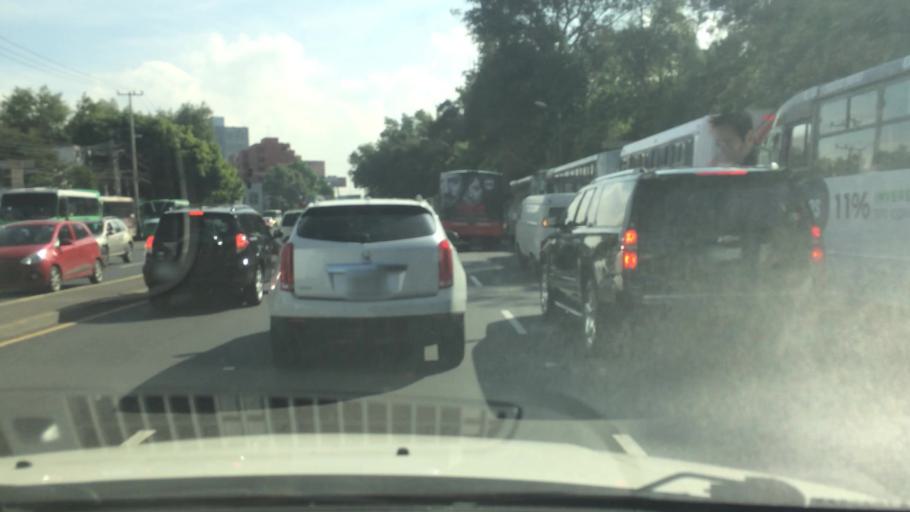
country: MX
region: Mexico City
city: Coyoacan
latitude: 19.3537
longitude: -99.1757
